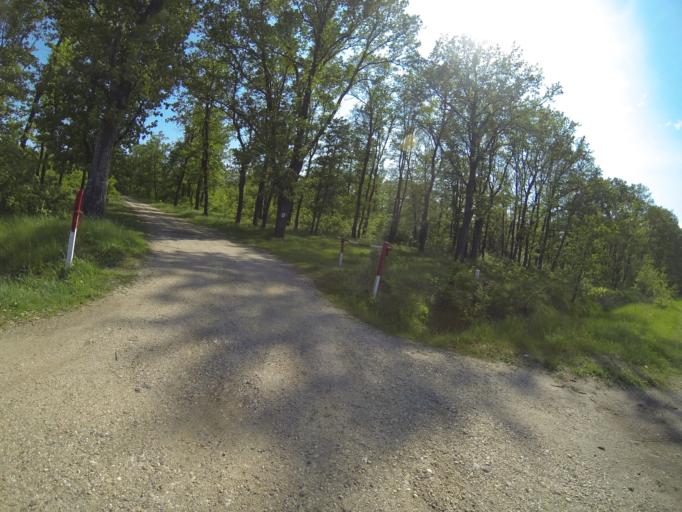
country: RO
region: Dolj
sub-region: Comuna Plenita
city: Castrele Traiane
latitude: 44.2548
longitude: 23.1464
